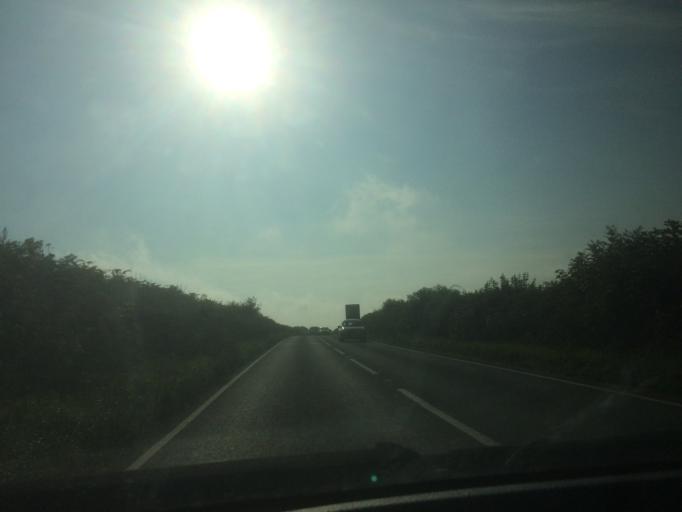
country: GB
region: England
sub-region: Cornwall
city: Callington
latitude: 50.4991
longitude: -4.3054
